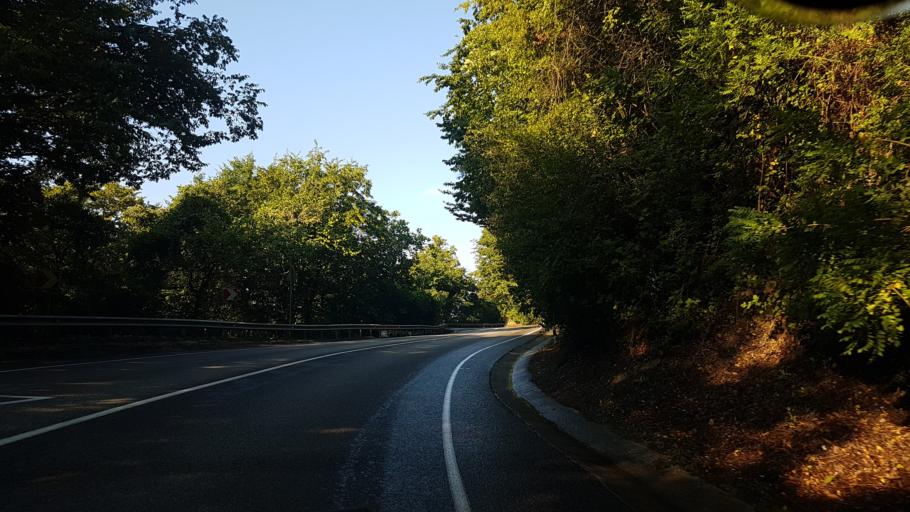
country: RU
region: Krasnodarskiy
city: Vardane
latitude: 43.8170
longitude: 39.4463
